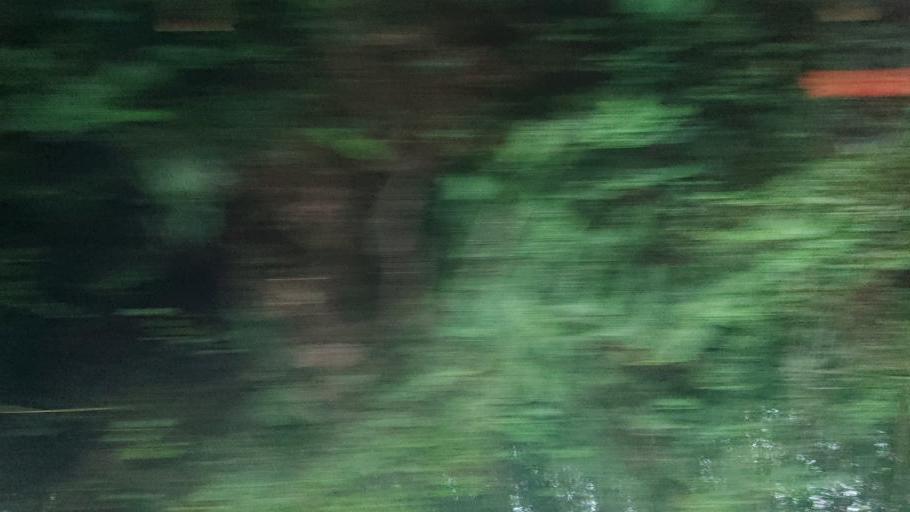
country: TW
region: Taiwan
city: Lugu
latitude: 23.5153
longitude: 120.6987
